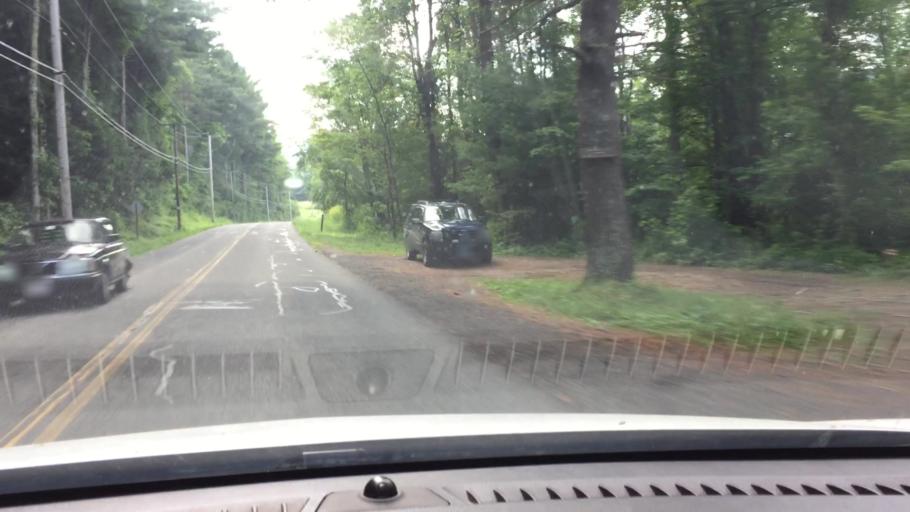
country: US
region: Massachusetts
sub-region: Berkshire County
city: Lee
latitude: 42.2355
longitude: -73.1944
